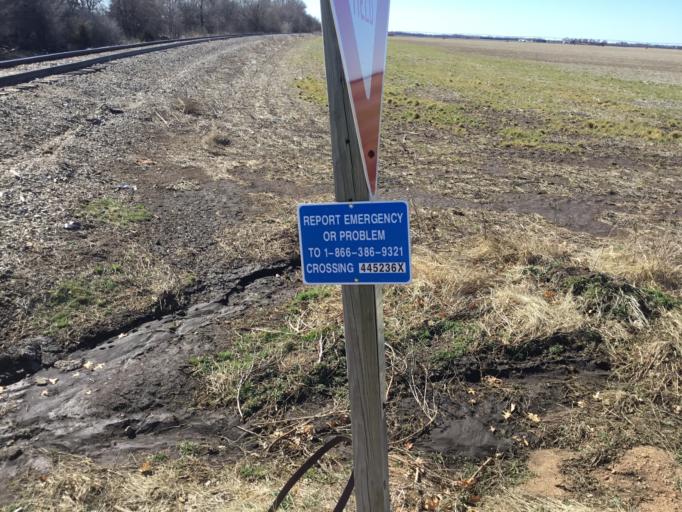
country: US
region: Kansas
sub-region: Reno County
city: Haven
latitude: 37.8541
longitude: -97.6562
